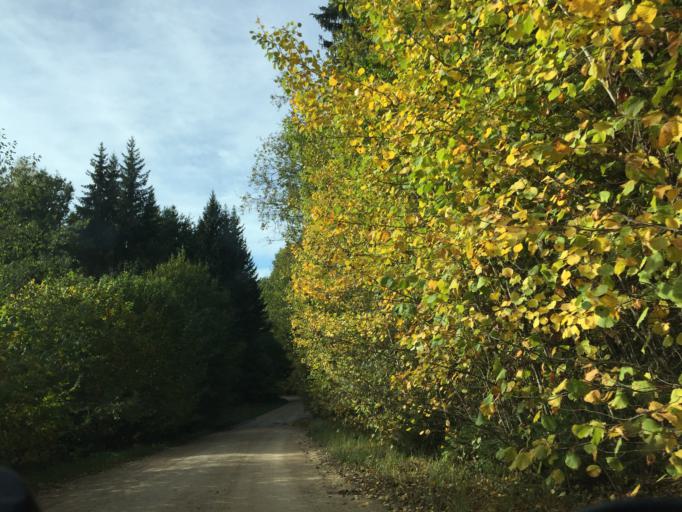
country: LV
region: Jaunpils
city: Jaunpils
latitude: 56.6140
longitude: 23.0194
